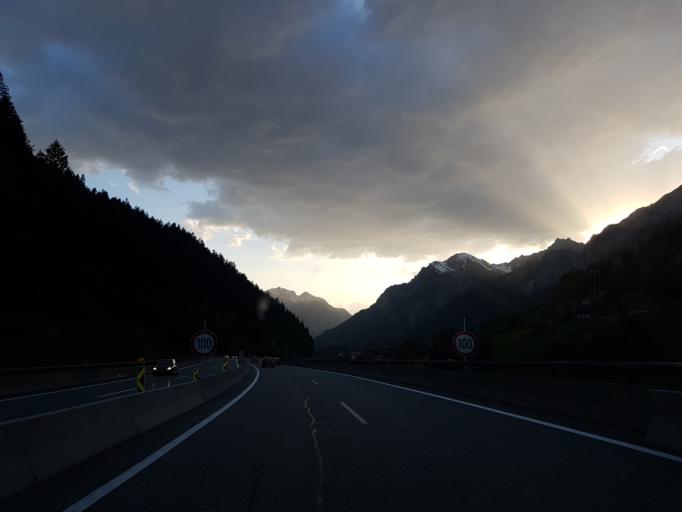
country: AT
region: Vorarlberg
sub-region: Politischer Bezirk Bludenz
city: Klosterle
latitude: 47.1306
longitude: 10.0793
